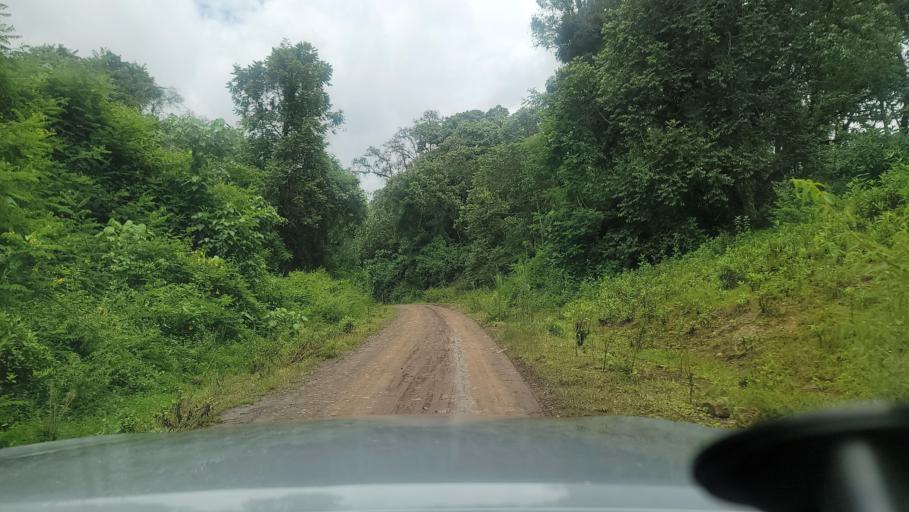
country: ET
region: Southern Nations, Nationalities, and People's Region
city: Bonga
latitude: 7.6385
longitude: 36.2326
